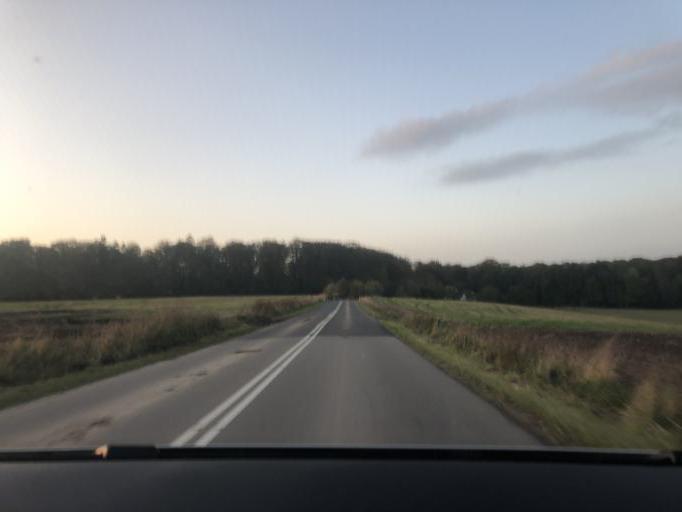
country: DK
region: Capital Region
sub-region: Egedal Kommune
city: Stenlose
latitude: 55.8064
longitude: 12.2114
